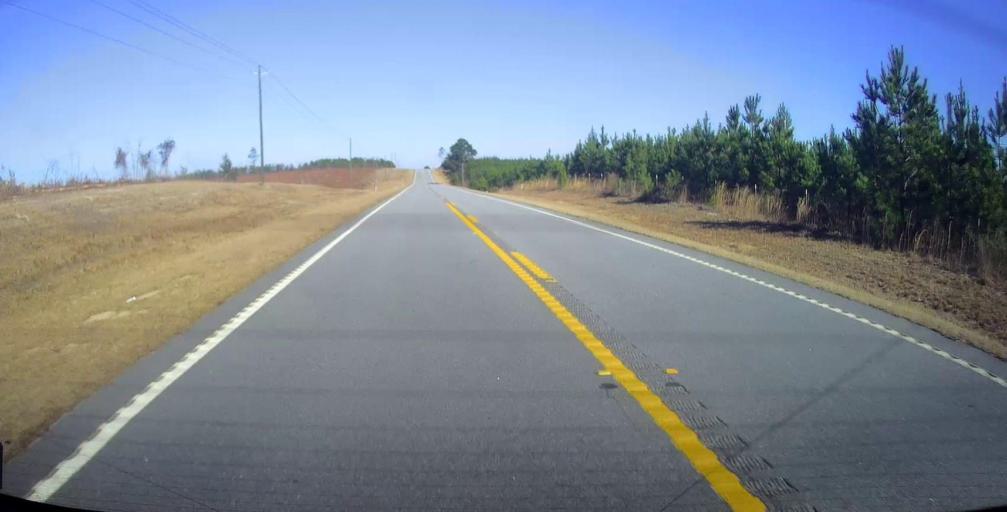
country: US
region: Georgia
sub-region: Taylor County
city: Butler
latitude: 32.5817
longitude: -84.2026
